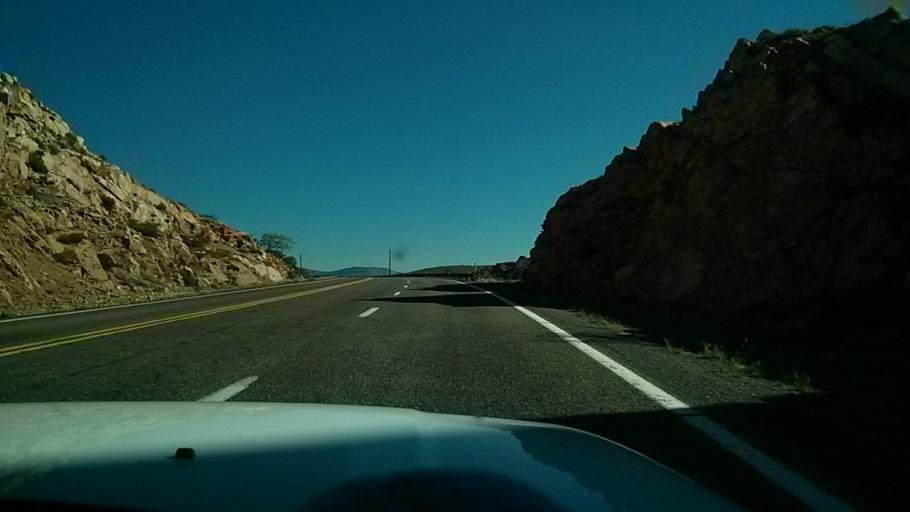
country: US
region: Arizona
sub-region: Mohave County
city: Peach Springs
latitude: 35.4124
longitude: -113.6472
